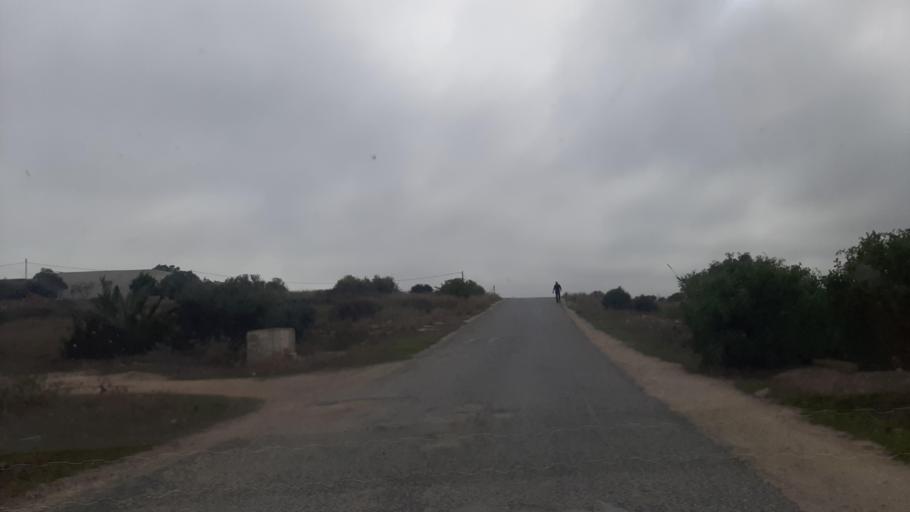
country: TN
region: Nabul
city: Menzel Heurr
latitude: 36.6733
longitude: 10.9200
